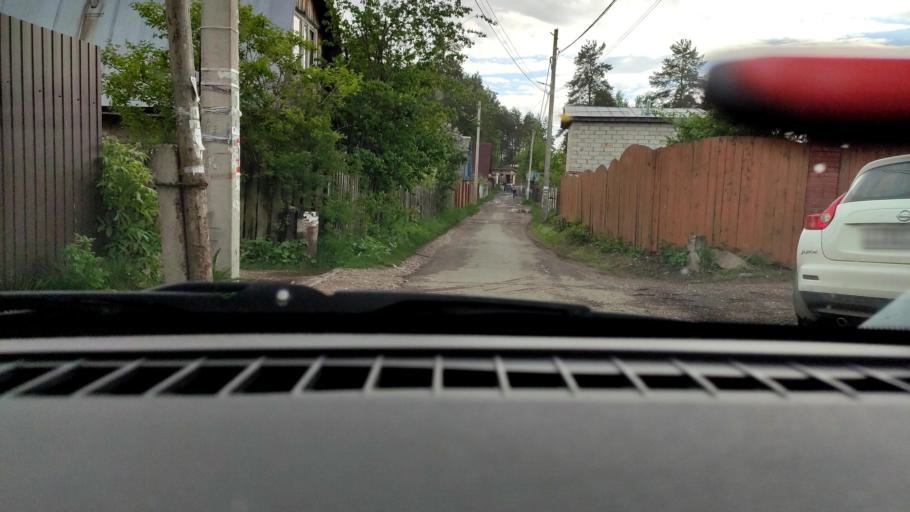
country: RU
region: Perm
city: Kondratovo
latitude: 58.0571
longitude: 56.1328
